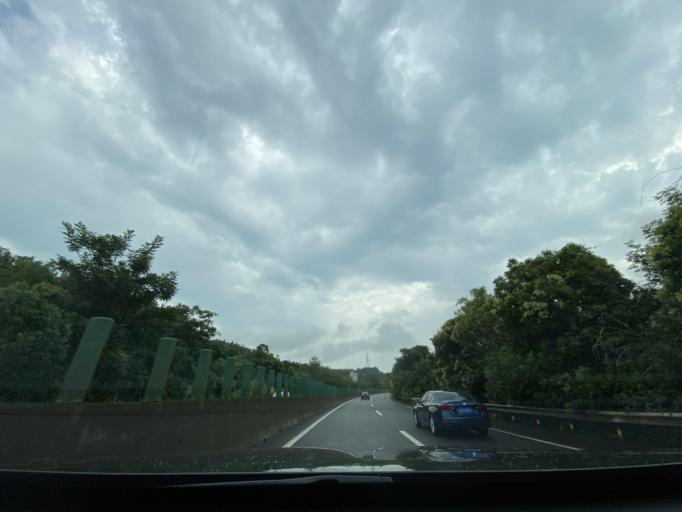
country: CN
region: Sichuan
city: Yanjiang
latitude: 30.1090
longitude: 104.6035
